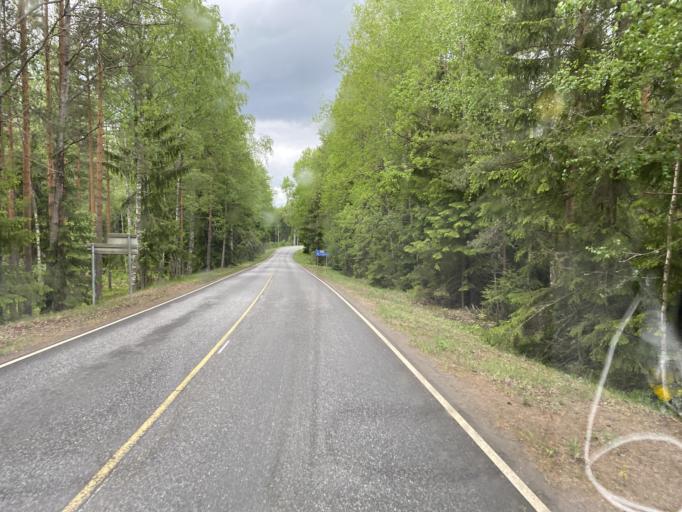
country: FI
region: Pirkanmaa
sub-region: Lounais-Pirkanmaa
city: Punkalaidun
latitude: 61.1019
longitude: 23.2764
